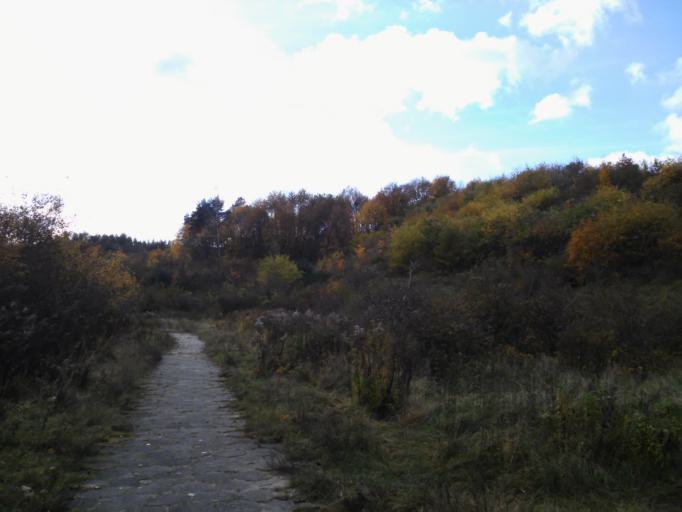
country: PL
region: Pomeranian Voivodeship
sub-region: Powiat gdanski
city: Kowale
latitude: 54.3681
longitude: 18.5789
